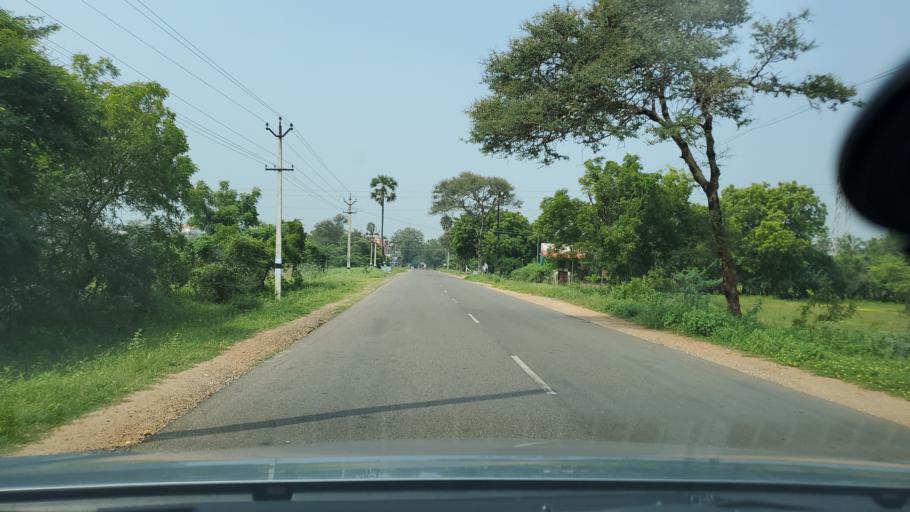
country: IN
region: Tamil Nadu
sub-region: Erode
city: Chennimalai
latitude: 11.1879
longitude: 77.6135
